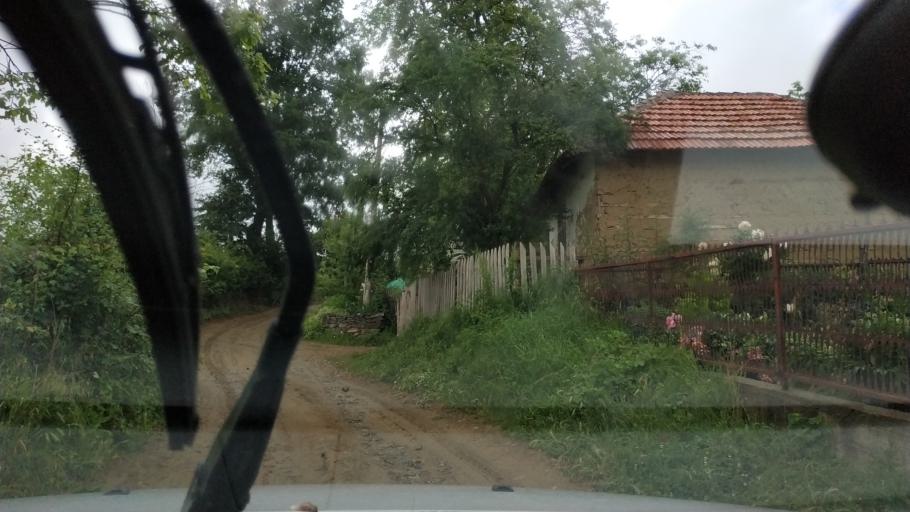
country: RS
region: Central Serbia
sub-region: Toplicki Okrug
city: Prokuplje
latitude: 43.3994
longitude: 21.5586
